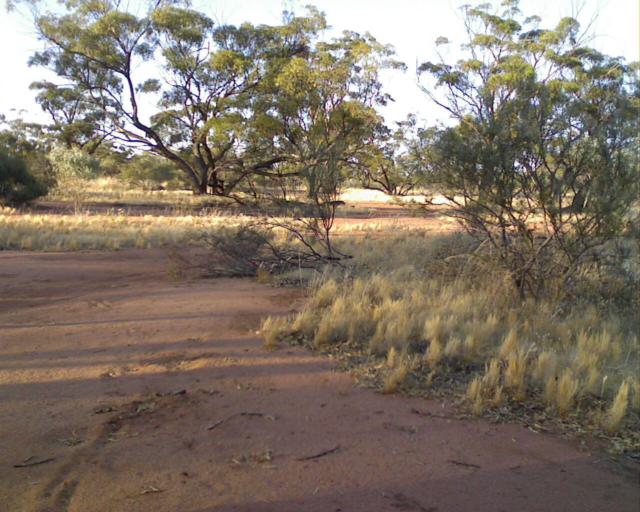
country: AU
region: Western Australia
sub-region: Merredin
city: Merredin
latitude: -30.8394
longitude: 117.9029
